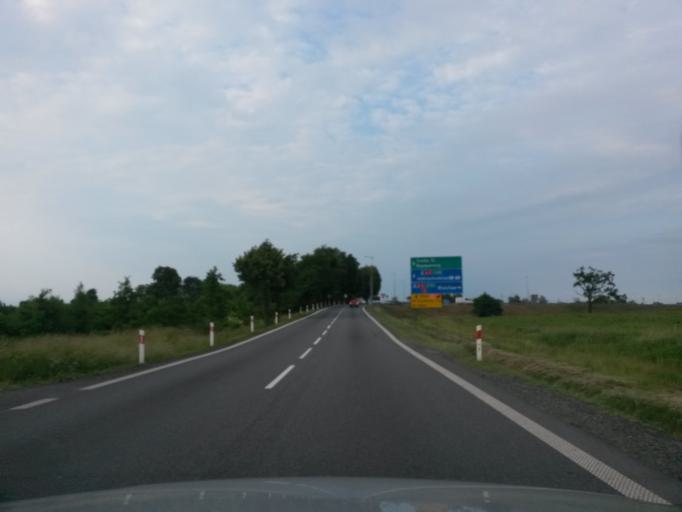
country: PL
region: Lower Silesian Voivodeship
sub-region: Powiat sredzki
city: Ciechow
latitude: 51.0417
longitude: 16.5908
